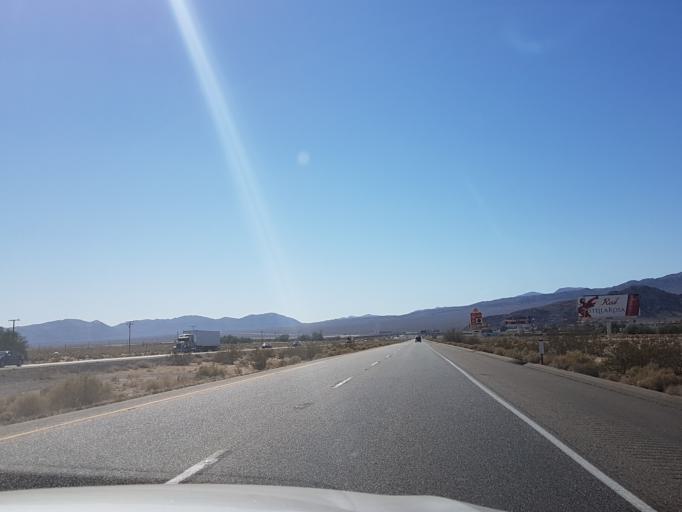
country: US
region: California
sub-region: San Bernardino County
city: Fort Irwin
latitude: 35.2705
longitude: -116.0624
